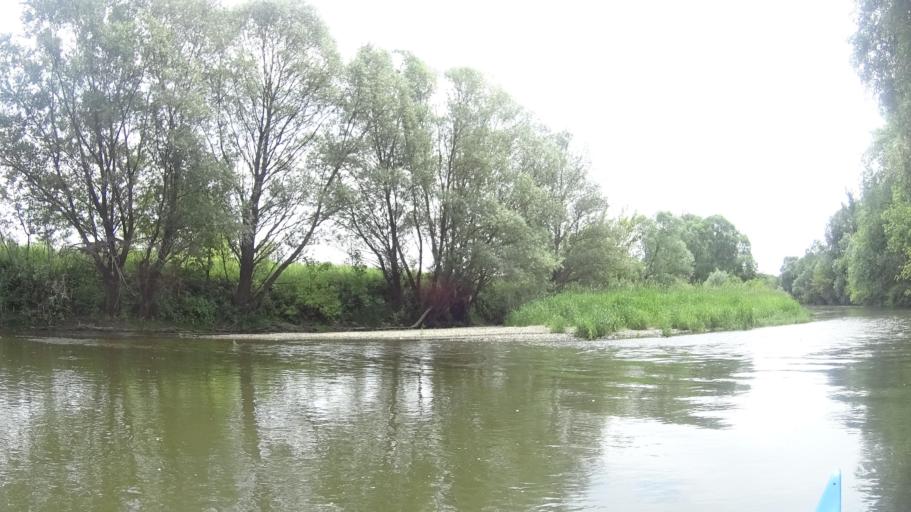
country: HU
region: Komarom-Esztergom
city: Esztergom
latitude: 47.9064
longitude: 18.7594
